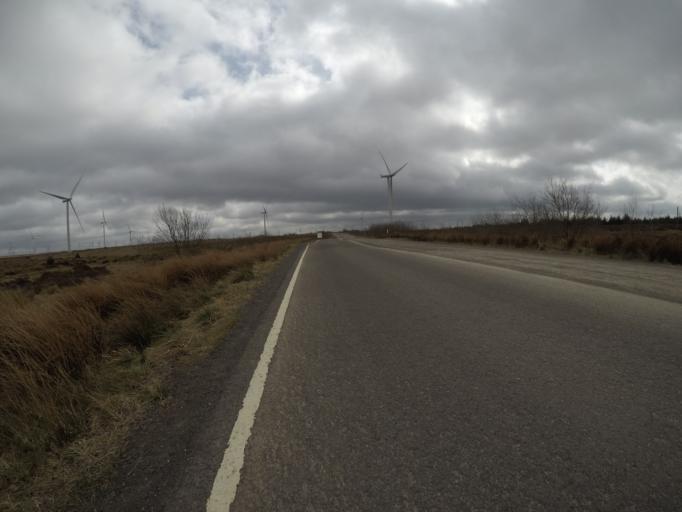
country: GB
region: Scotland
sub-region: East Renfrewshire
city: Newton Mearns
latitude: 55.7055
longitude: -4.3577
